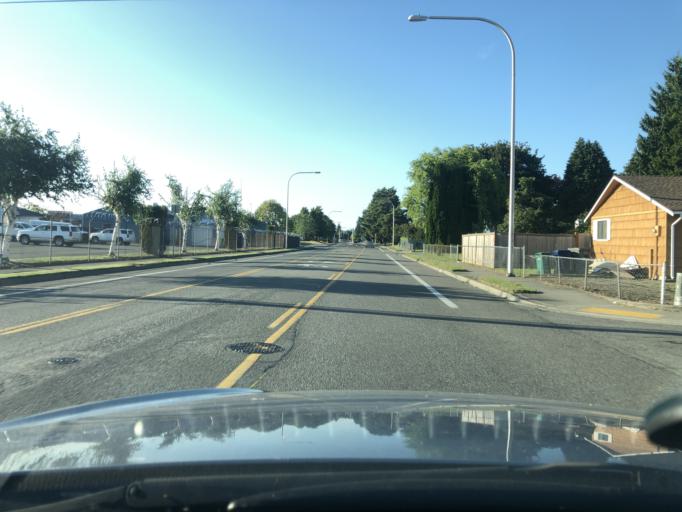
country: US
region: Washington
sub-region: King County
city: Auburn
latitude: 47.3221
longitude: -122.2191
